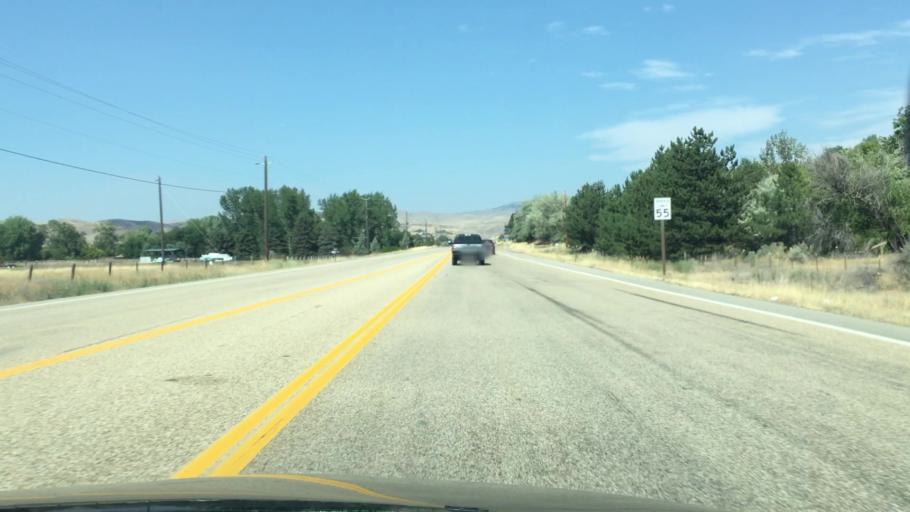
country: US
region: Idaho
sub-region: Ada County
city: Eagle
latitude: 43.7228
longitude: -116.3168
